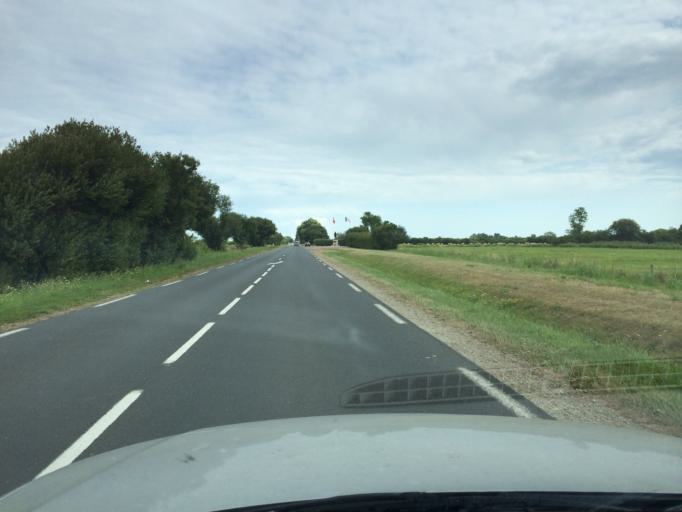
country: FR
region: Lower Normandy
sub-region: Departement de la Manche
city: Saint-Hilaire-Petitville
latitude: 49.4021
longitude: -1.1977
